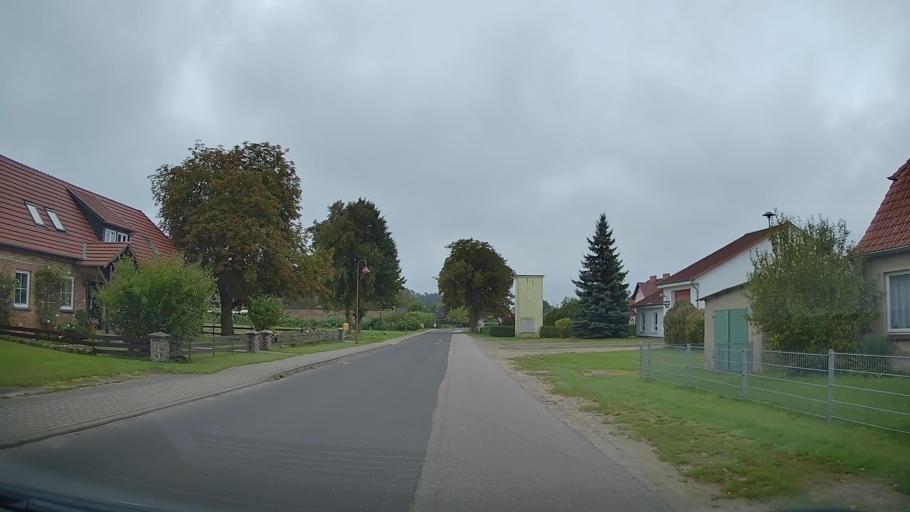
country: DE
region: Mecklenburg-Vorpommern
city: Kavelstorf
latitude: 53.9462
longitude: 12.2142
